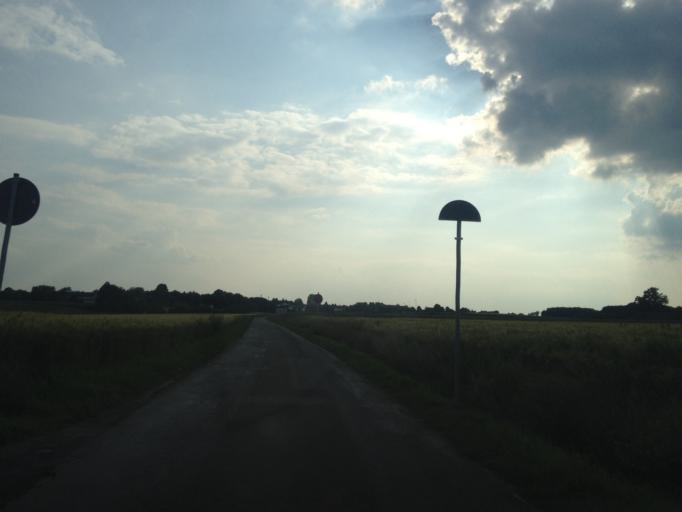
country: DE
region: North Rhine-Westphalia
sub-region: Regierungsbezirk Detmold
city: Rodinghausen
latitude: 52.2517
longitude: 8.5144
